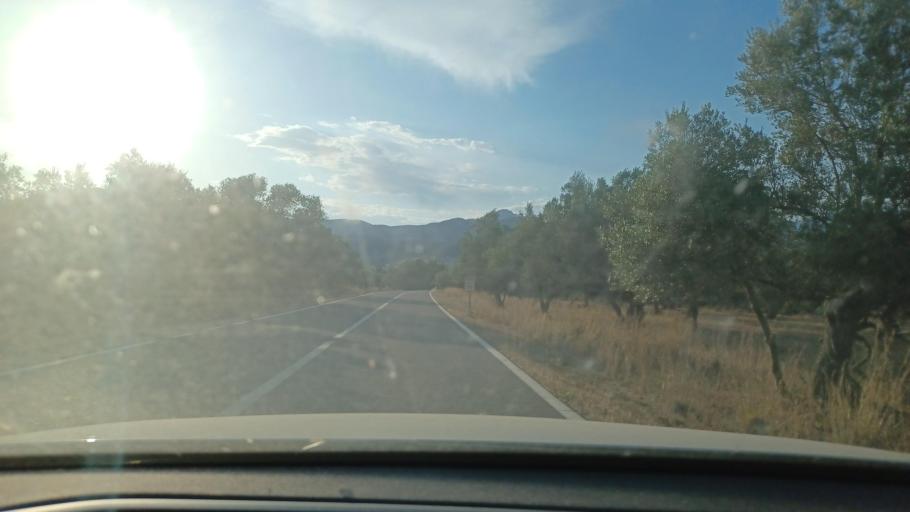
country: ES
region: Catalonia
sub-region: Provincia de Tarragona
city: Mas de Barberans
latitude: 40.7259
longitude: 0.3883
